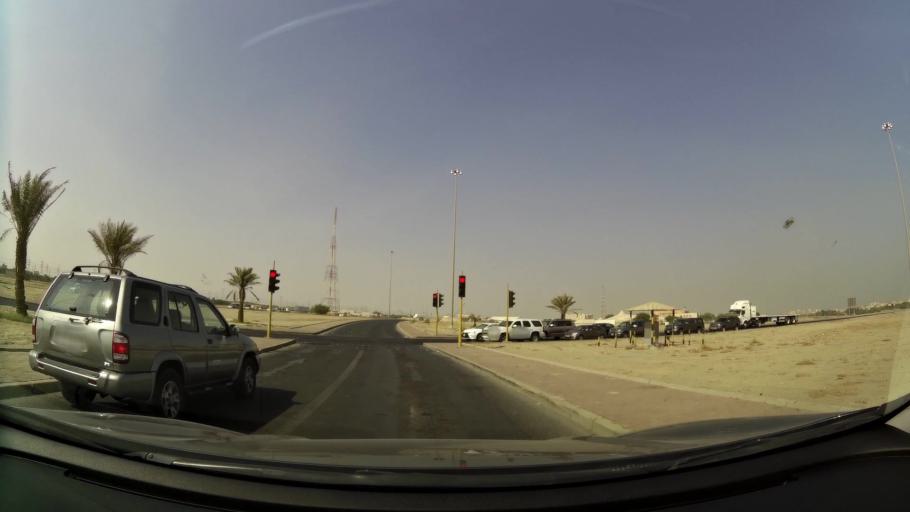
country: KW
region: Al Ahmadi
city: Al Fahahil
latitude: 29.0748
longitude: 48.1095
